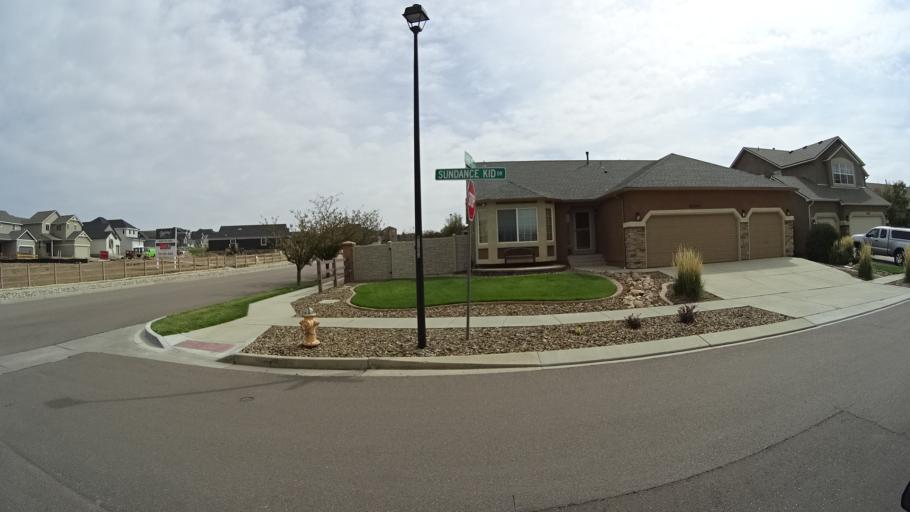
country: US
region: Colorado
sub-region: El Paso County
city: Cimarron Hills
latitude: 38.9234
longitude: -104.6902
